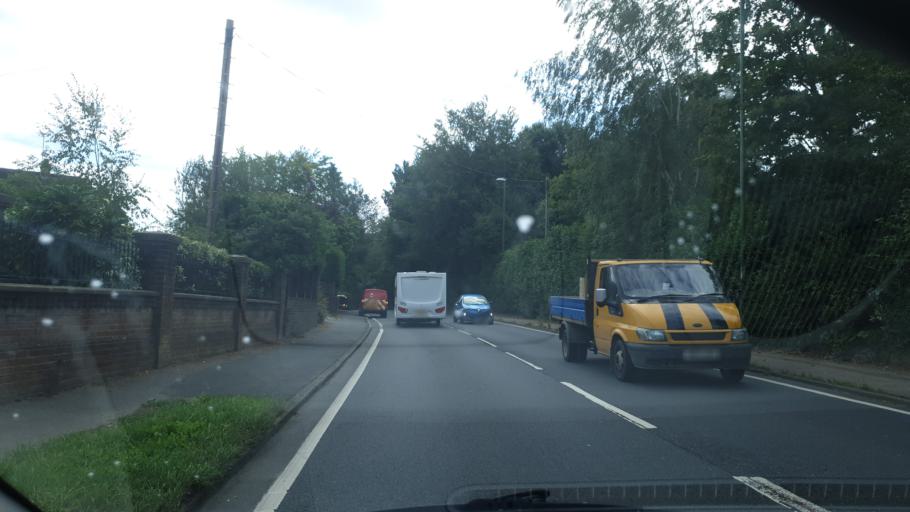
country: GB
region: England
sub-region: West Sussex
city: East Grinstead
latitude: 51.1213
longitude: 0.0067
